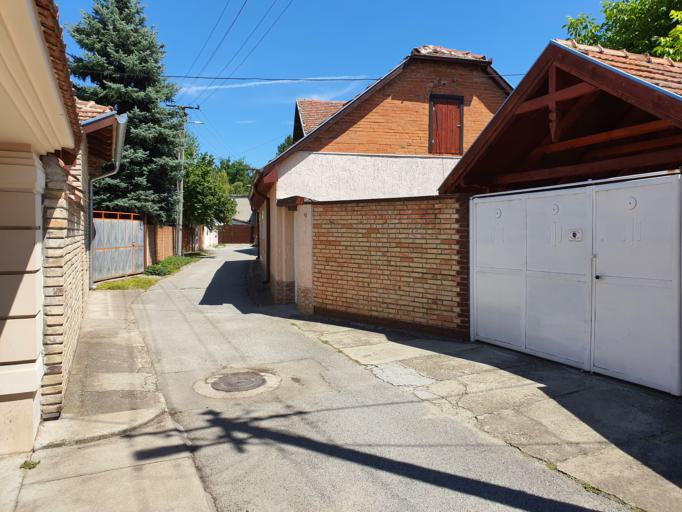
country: RS
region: Autonomna Pokrajina Vojvodina
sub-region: Severnobacki Okrug
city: Subotica
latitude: 46.1028
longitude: 19.6562
